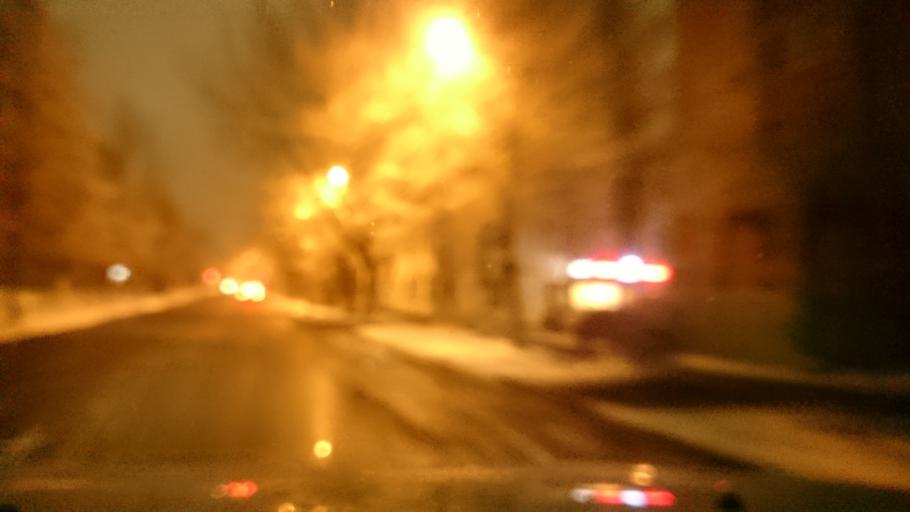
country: RU
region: Tula
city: Mendeleyevskiy
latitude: 54.1681
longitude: 37.5817
